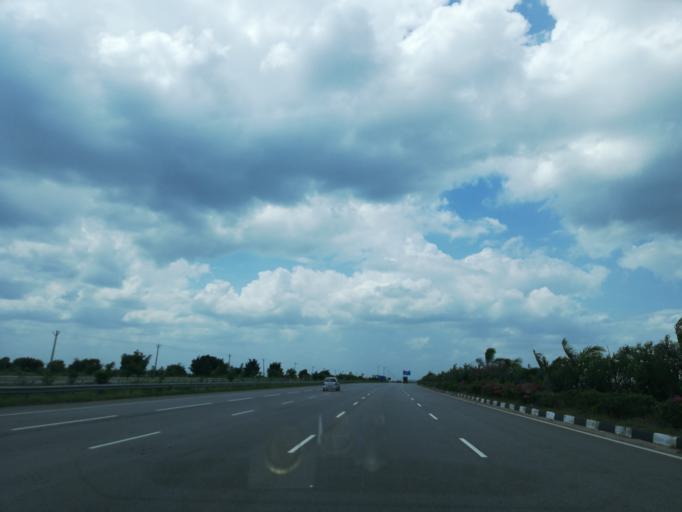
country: IN
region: Telangana
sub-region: Medak
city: Serilingampalle
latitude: 17.4564
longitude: 78.2516
